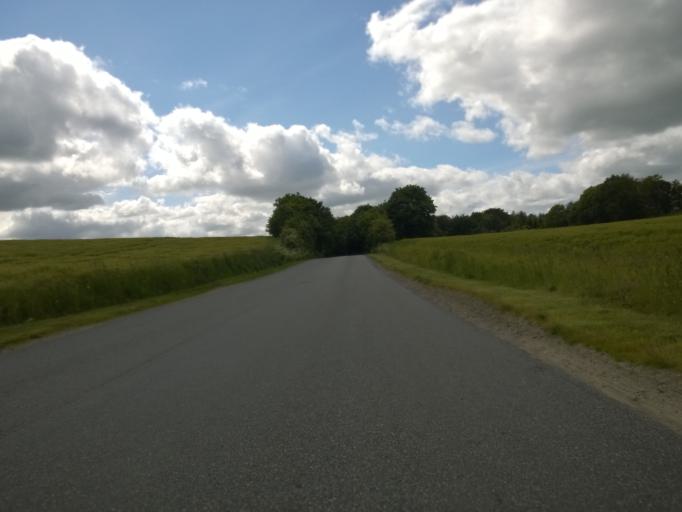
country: DK
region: Central Jutland
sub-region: Holstebro Kommune
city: Vinderup
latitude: 56.4041
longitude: 8.7681
